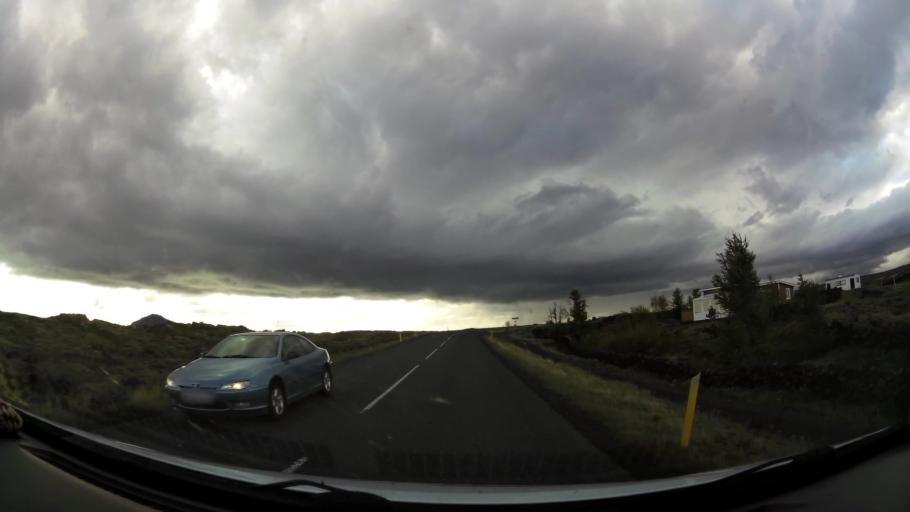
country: IS
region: Northeast
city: Laugar
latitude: 65.6449
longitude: -16.9177
